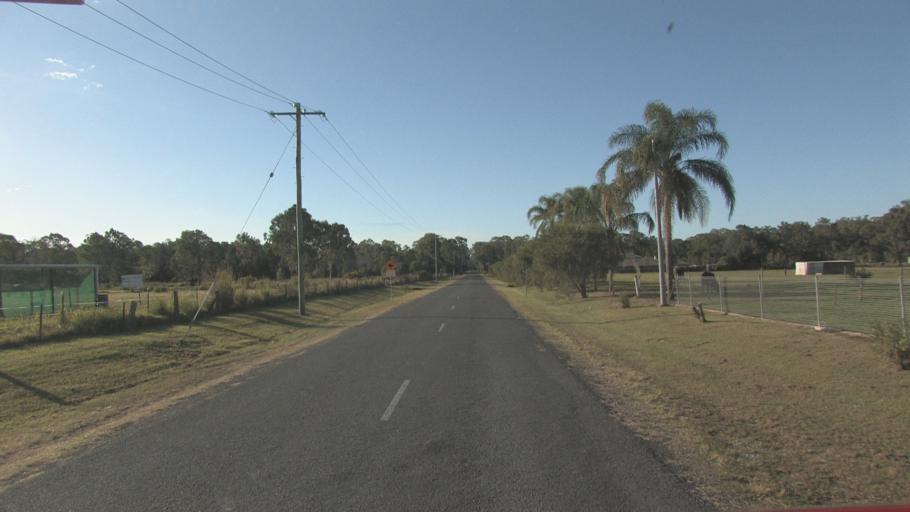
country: AU
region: Queensland
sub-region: Gold Coast
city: Yatala
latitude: -27.6780
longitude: 153.2427
